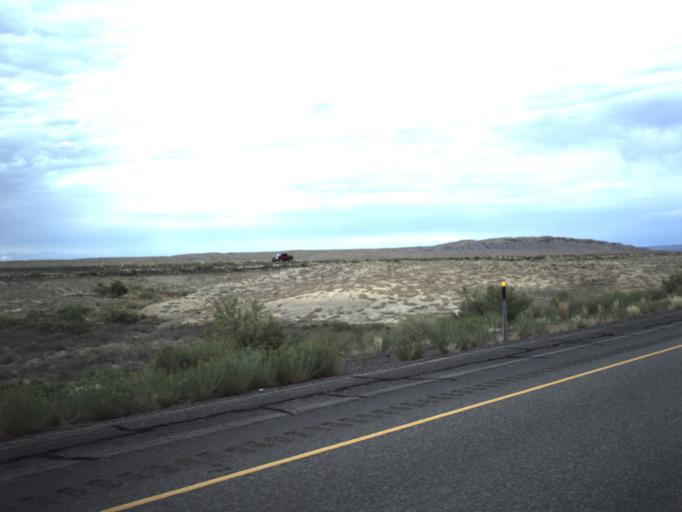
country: US
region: Utah
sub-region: Grand County
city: Moab
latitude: 38.9389
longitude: -109.5031
